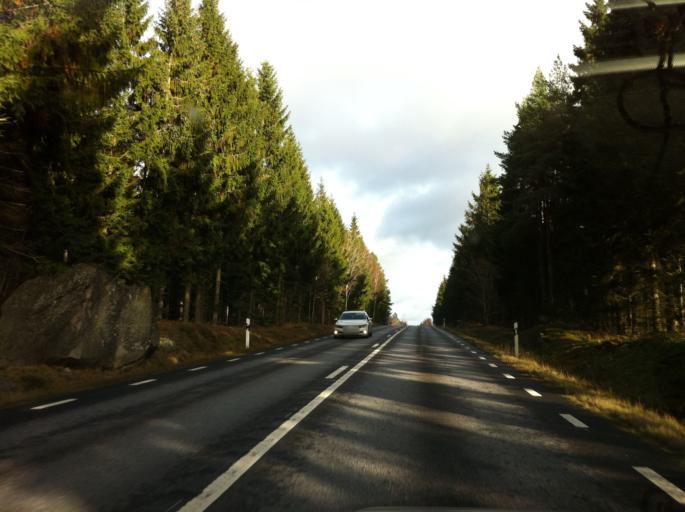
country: SE
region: Kronoberg
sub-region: Alvesta Kommun
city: Vislanda
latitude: 56.7387
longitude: 14.5059
